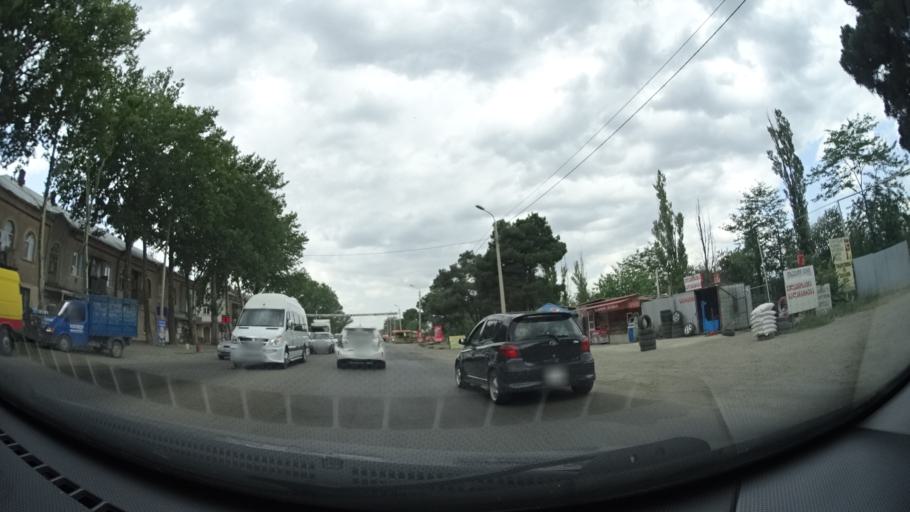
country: GE
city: Didi Lilo
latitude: 41.6921
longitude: 44.9801
